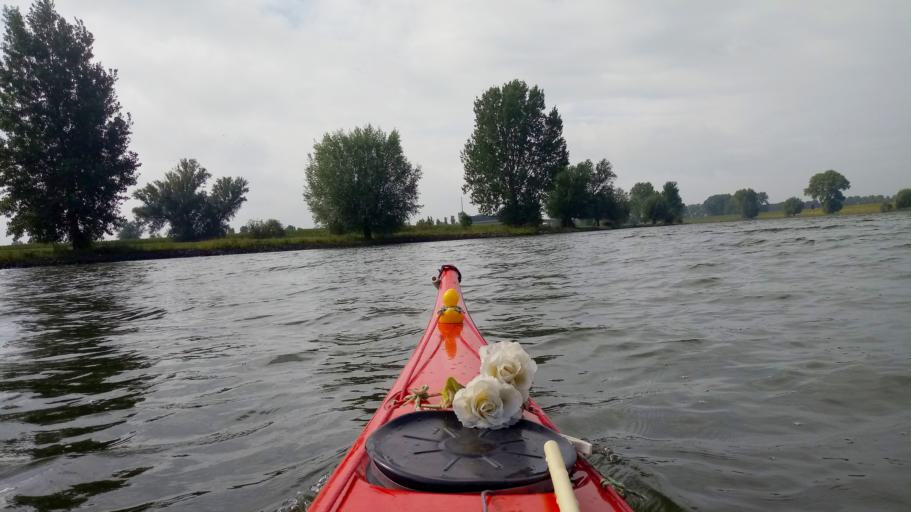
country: NL
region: North Brabant
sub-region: Gemeente Aalburg
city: Aalburg
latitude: 51.7475
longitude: 5.1318
